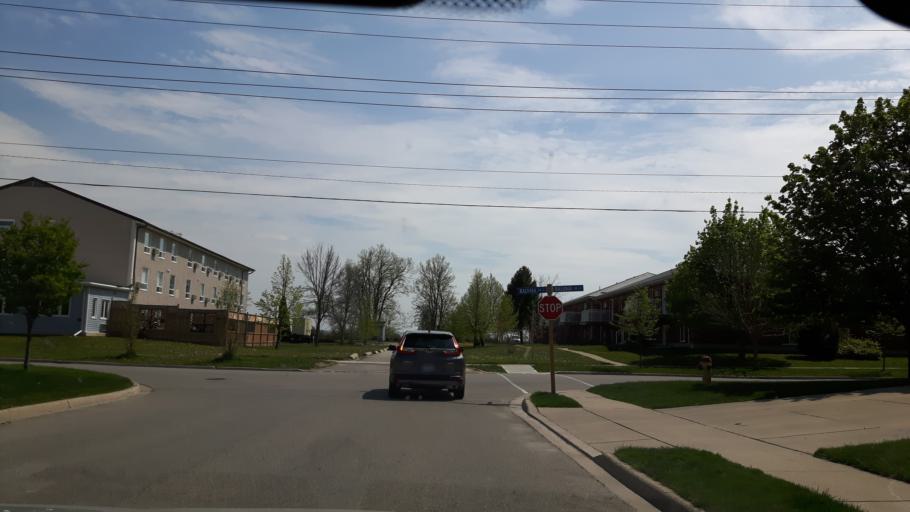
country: CA
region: Ontario
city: Goderich
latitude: 43.7292
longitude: -81.7100
